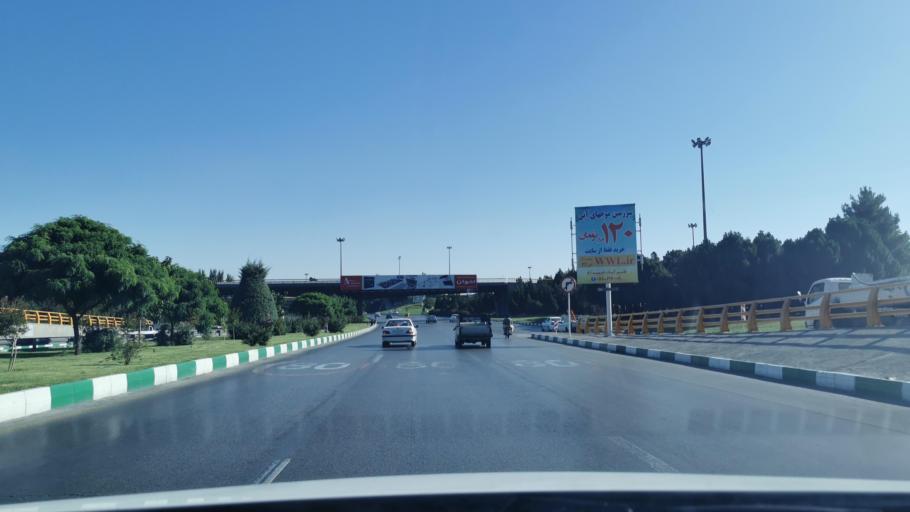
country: IR
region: Razavi Khorasan
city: Mashhad
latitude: 36.3417
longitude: 59.5477
